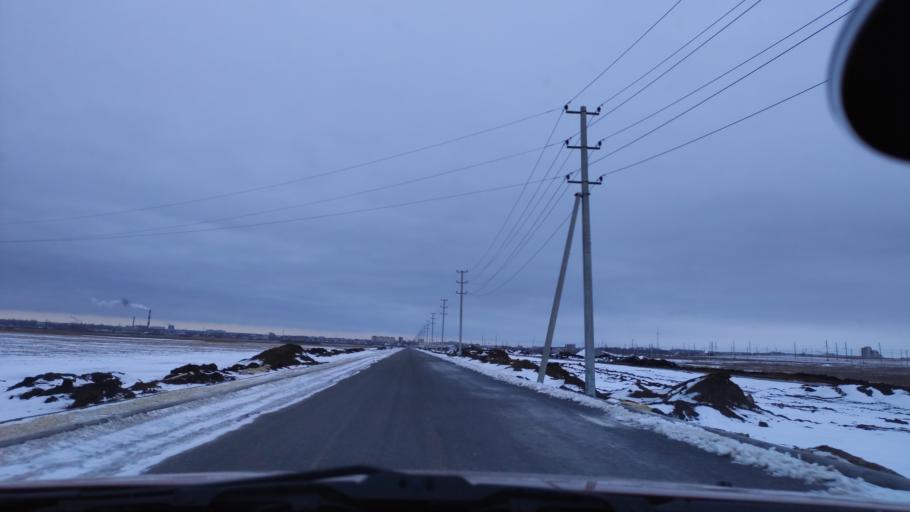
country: RU
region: Tambov
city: Donskoye
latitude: 52.7835
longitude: 41.4335
